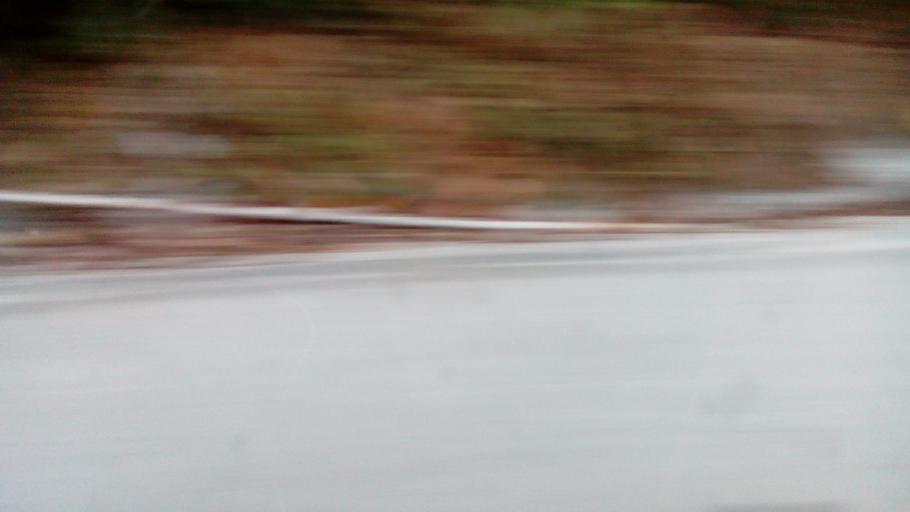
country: TW
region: Taiwan
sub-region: Hualien
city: Hualian
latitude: 24.3293
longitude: 121.3101
